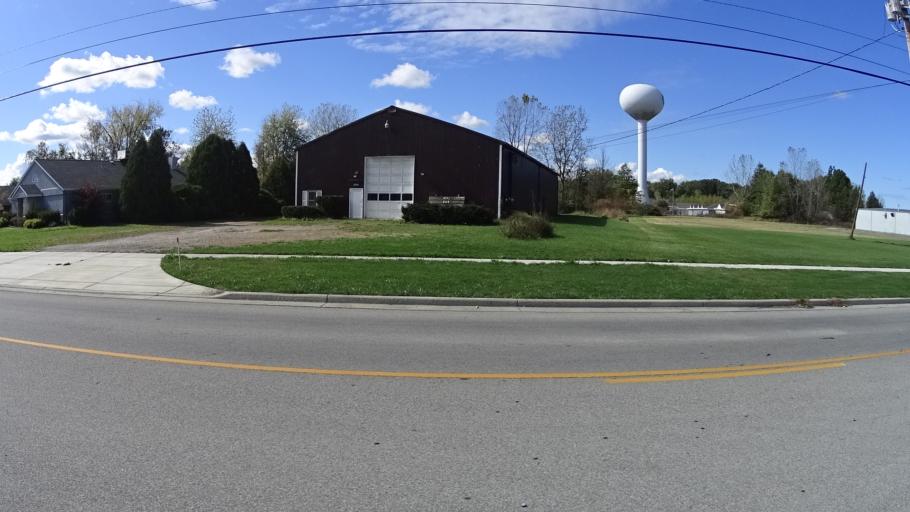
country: US
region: Ohio
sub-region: Lorain County
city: Grafton
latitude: 41.2865
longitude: -82.0644
